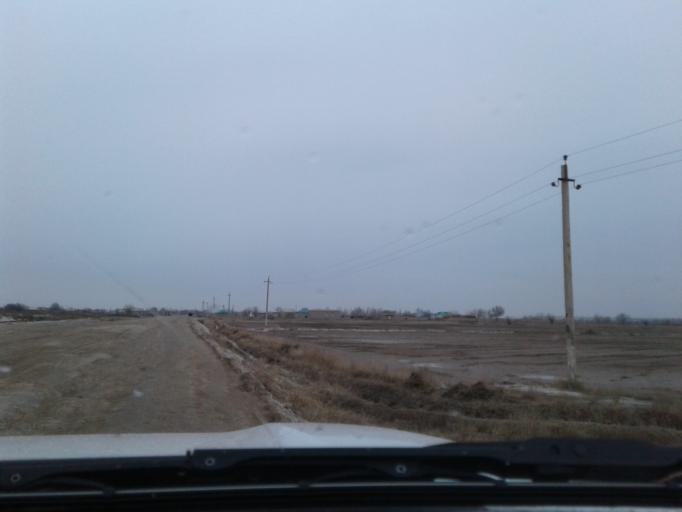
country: UZ
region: Karakalpakstan
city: Shumanay Shahri
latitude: 42.2806
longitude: 58.6441
